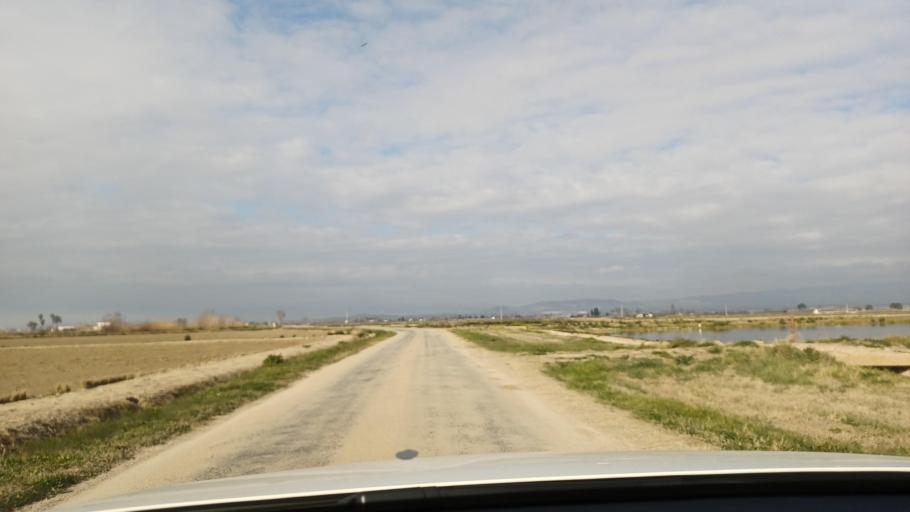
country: ES
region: Catalonia
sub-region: Provincia de Tarragona
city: Deltebre
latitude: 40.6976
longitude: 0.6469
